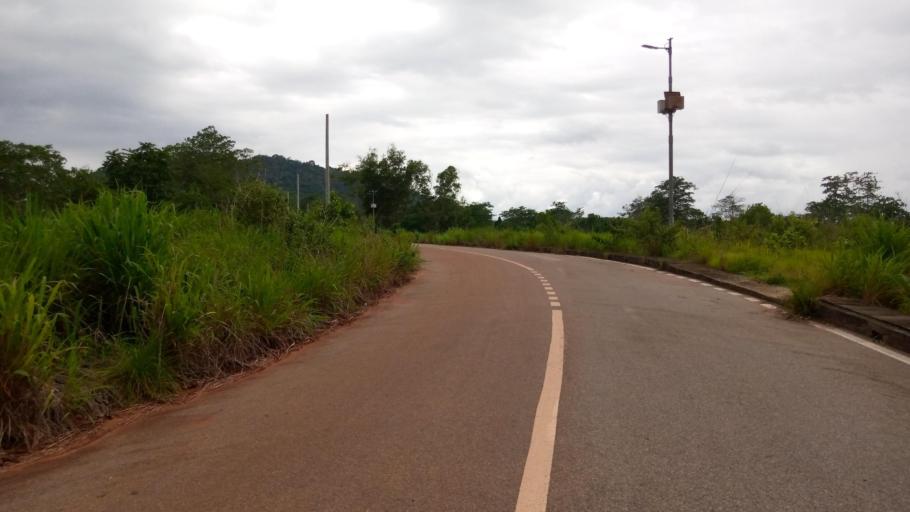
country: SL
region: Southern Province
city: Moyamba
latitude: 8.1604
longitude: -12.4435
